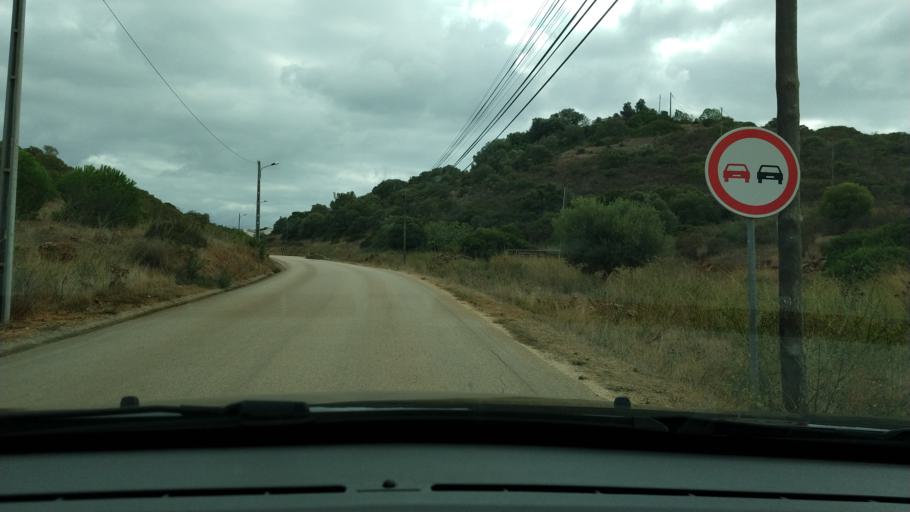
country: PT
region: Faro
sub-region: Lagos
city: Lagos
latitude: 37.0821
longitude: -8.7773
